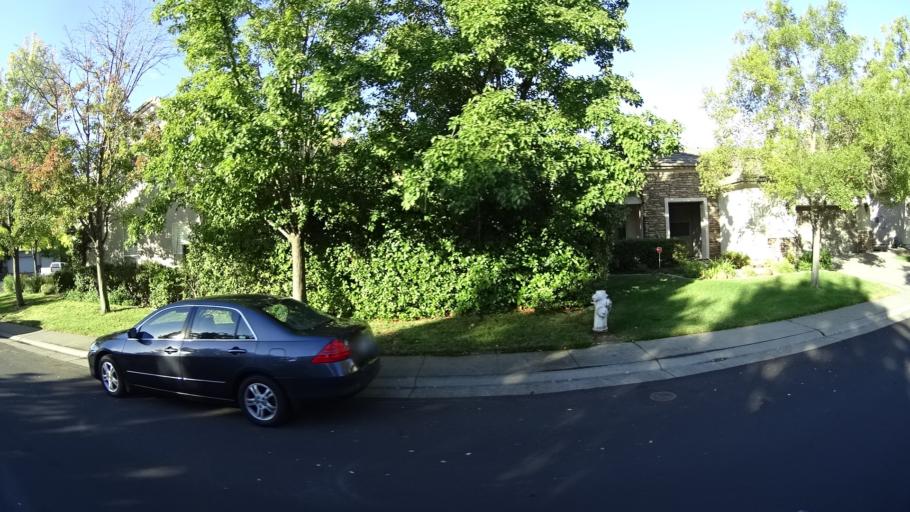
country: US
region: California
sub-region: Sacramento County
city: Laguna
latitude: 38.4015
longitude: -121.4772
